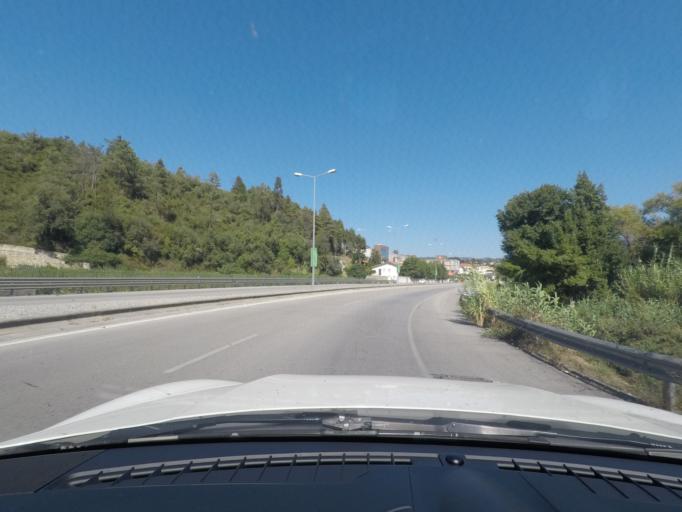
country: PT
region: Coimbra
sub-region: Coimbra
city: Coimbra
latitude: 40.2232
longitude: -8.4267
